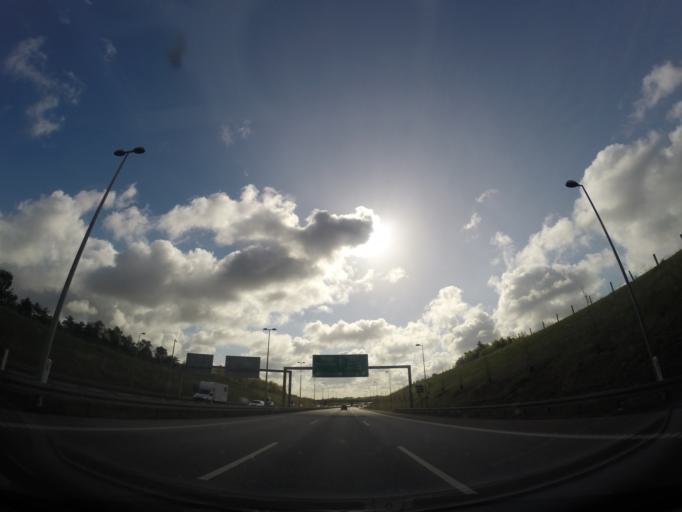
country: DK
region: Capital Region
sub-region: Glostrup Kommune
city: Glostrup
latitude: 55.6946
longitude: 12.3962
